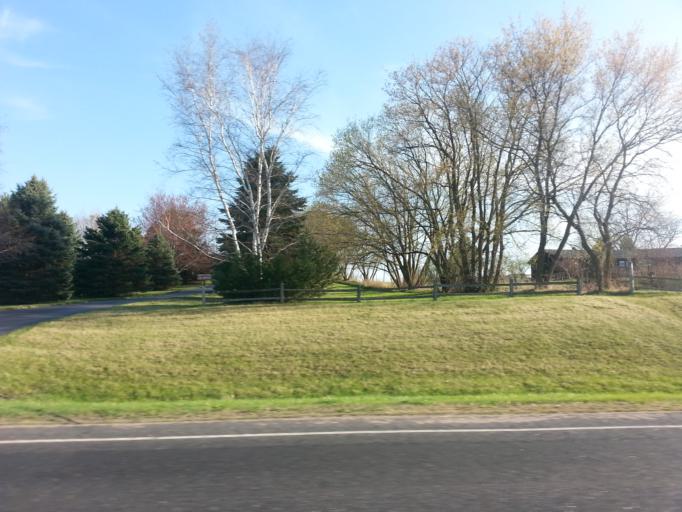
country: US
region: Minnesota
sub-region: Washington County
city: Afton
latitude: 44.8258
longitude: -92.7309
